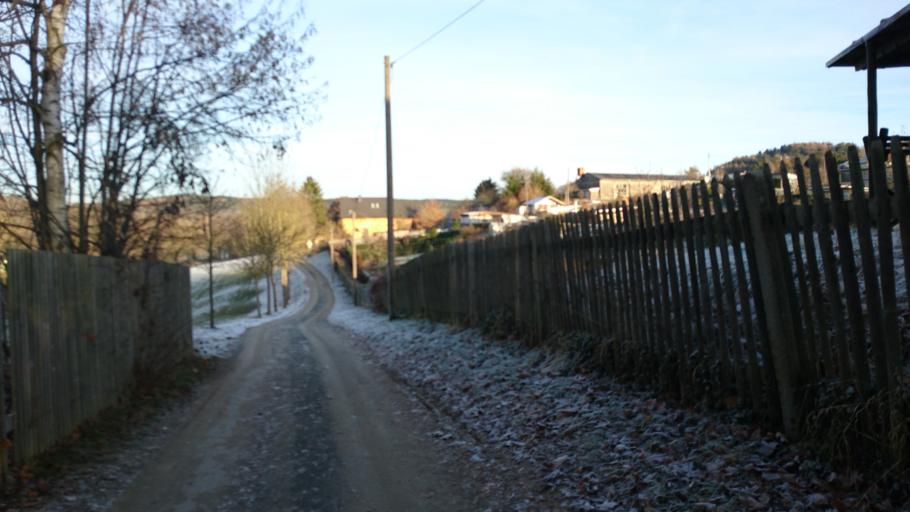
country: DE
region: Thuringia
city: Schleiz
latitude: 50.5809
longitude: 11.8210
